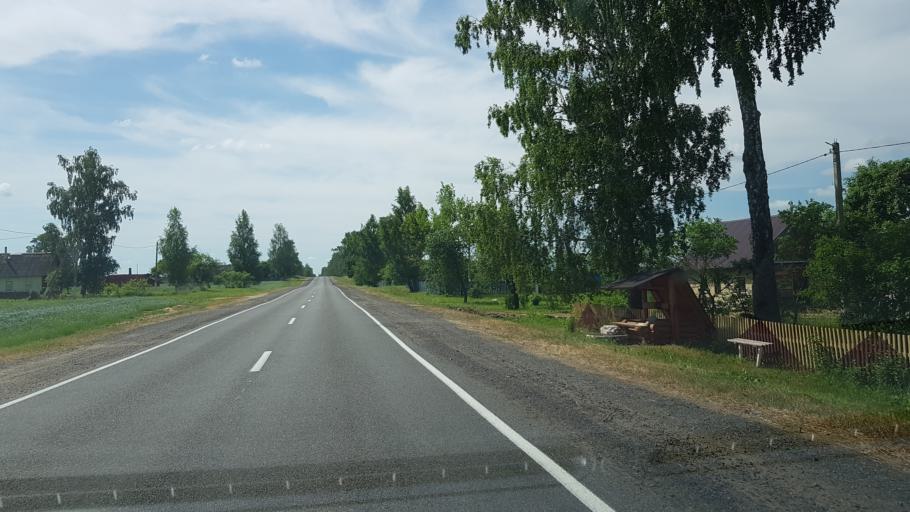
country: BY
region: Vitebsk
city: Dubrowna
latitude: 54.6108
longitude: 30.6719
